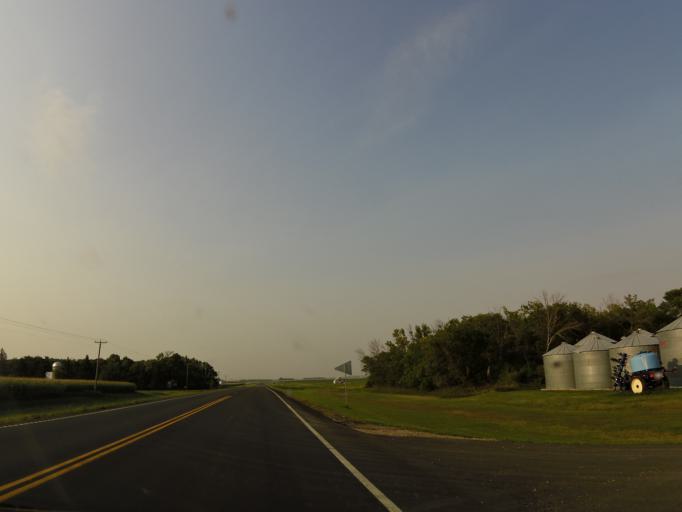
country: US
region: North Dakota
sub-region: Traill County
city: Mayville
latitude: 47.3584
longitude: -97.3258
